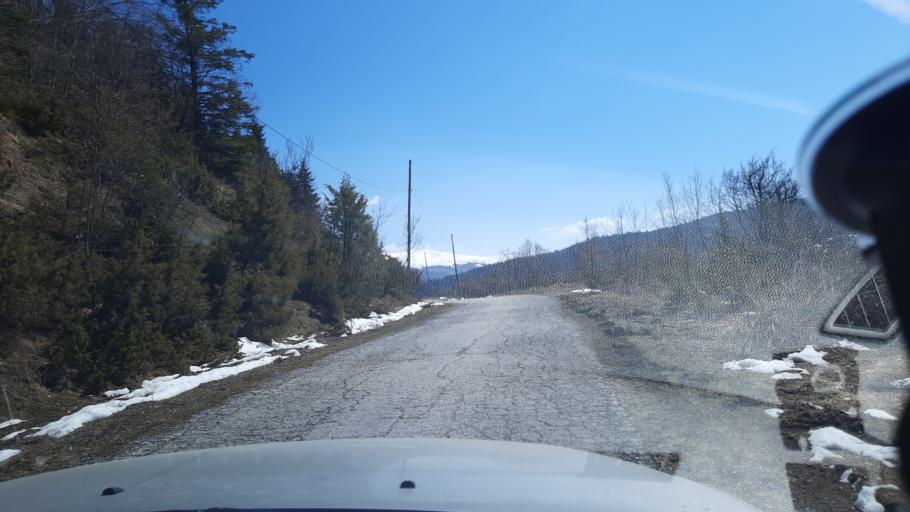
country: MK
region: Gostivar
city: Vrutok
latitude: 41.7113
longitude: 20.7314
